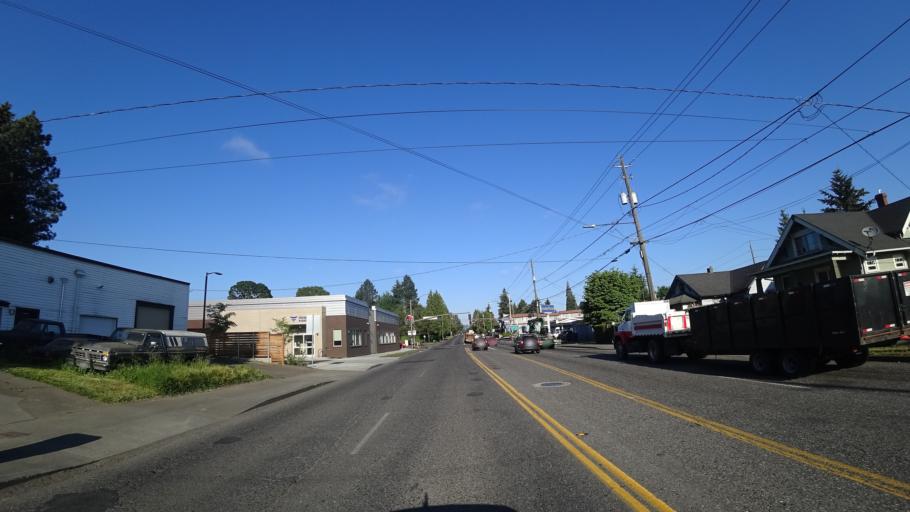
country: US
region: Oregon
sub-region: Multnomah County
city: Portland
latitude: 45.5772
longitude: -122.6602
